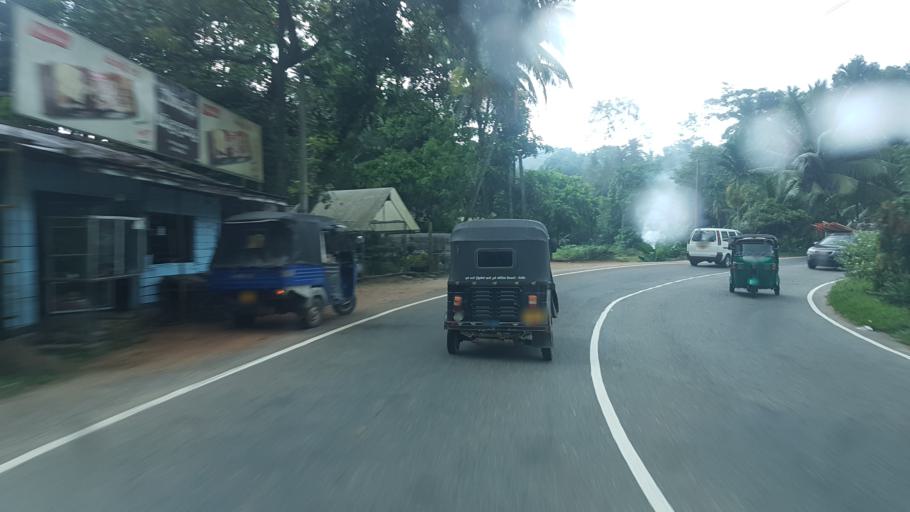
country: LK
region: Western
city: Hanwella Ihala
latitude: 6.9639
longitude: 80.2295
